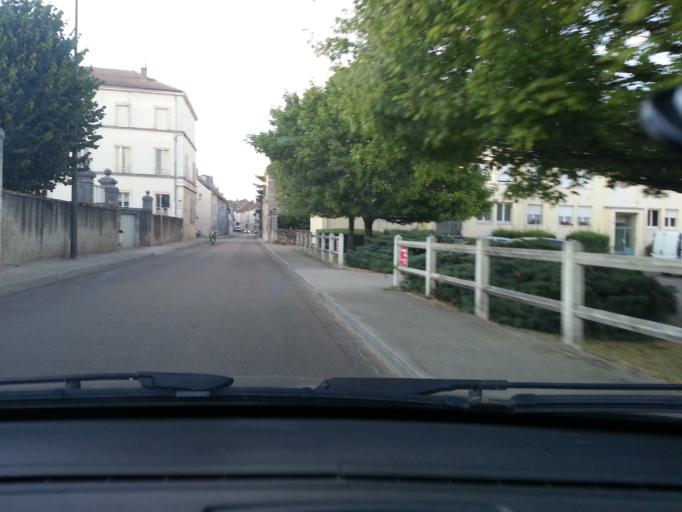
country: FR
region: Bourgogne
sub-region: Departement de Saone-et-Loire
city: Givry
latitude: 46.7804
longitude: 4.7412
